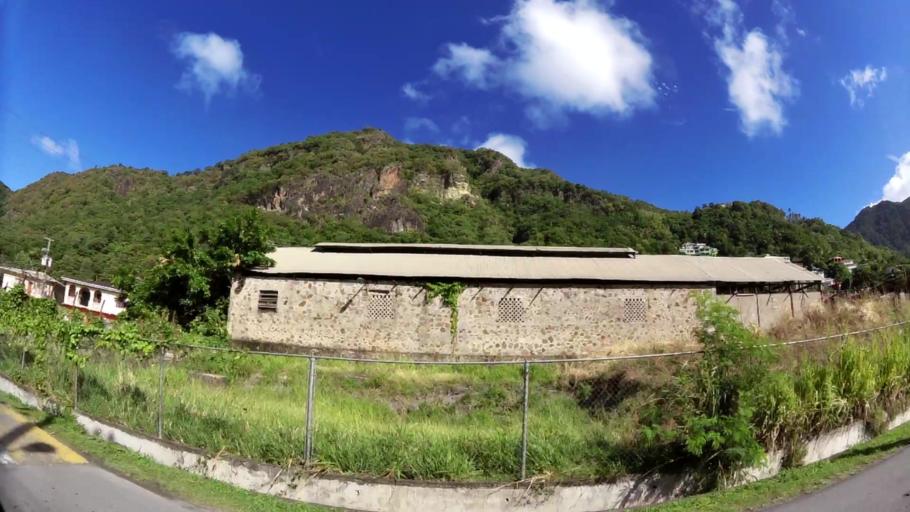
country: LC
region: Soufriere
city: Soufriere
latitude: 13.8577
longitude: -61.0573
